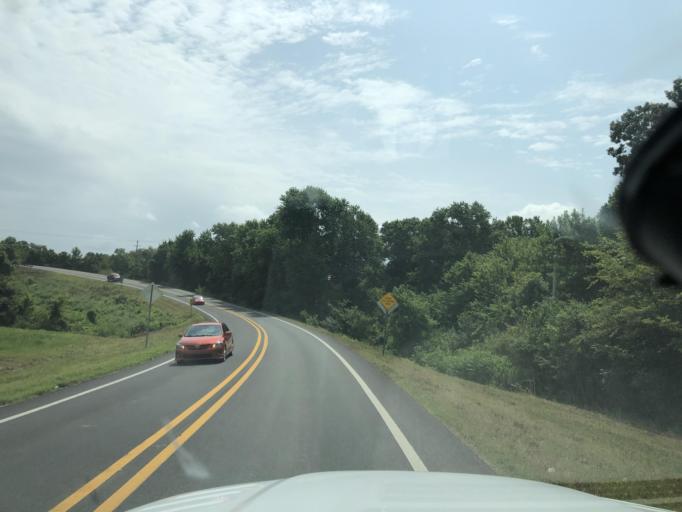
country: US
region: Arkansas
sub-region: Yell County
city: Danville
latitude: 35.0653
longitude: -93.3947
